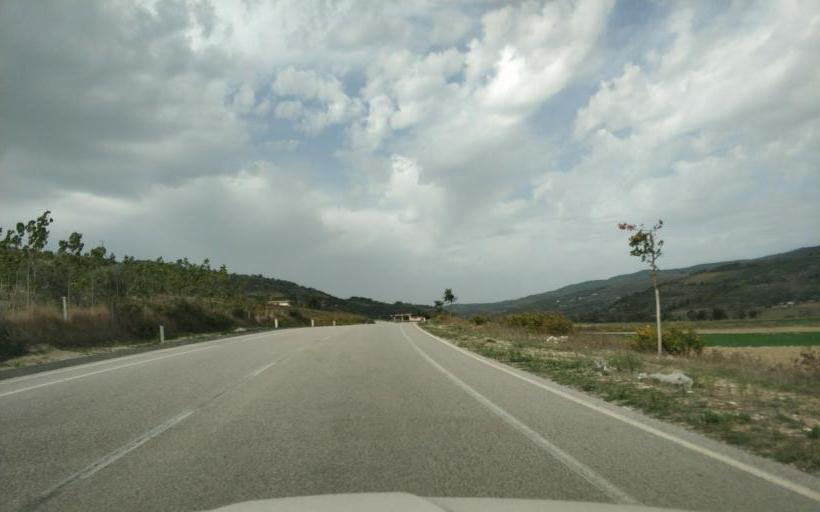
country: AL
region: Gjirokaster
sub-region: Rrethi i Tepelenes
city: Krahes
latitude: 40.4457
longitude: 19.8486
